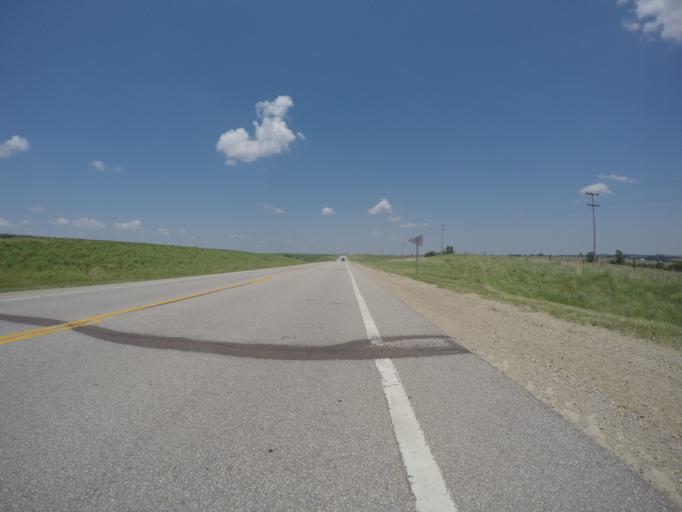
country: US
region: Kansas
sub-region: Doniphan County
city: Troy
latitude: 39.7428
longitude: -95.1438
